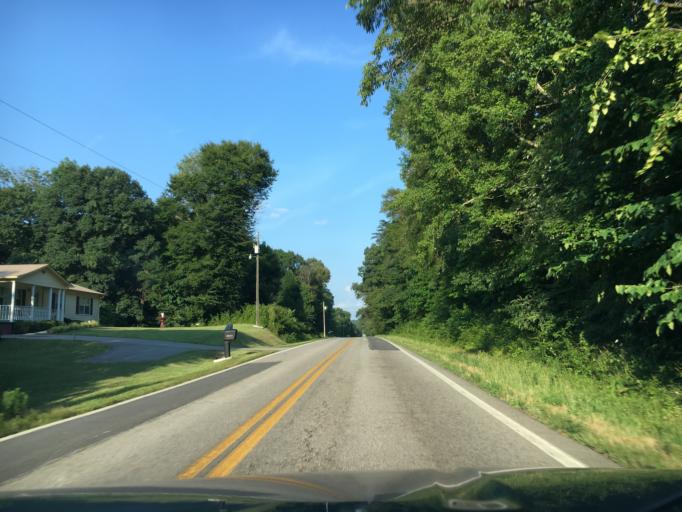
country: US
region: Virginia
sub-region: Pittsylvania County
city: Chatham
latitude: 36.8281
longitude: -79.3103
